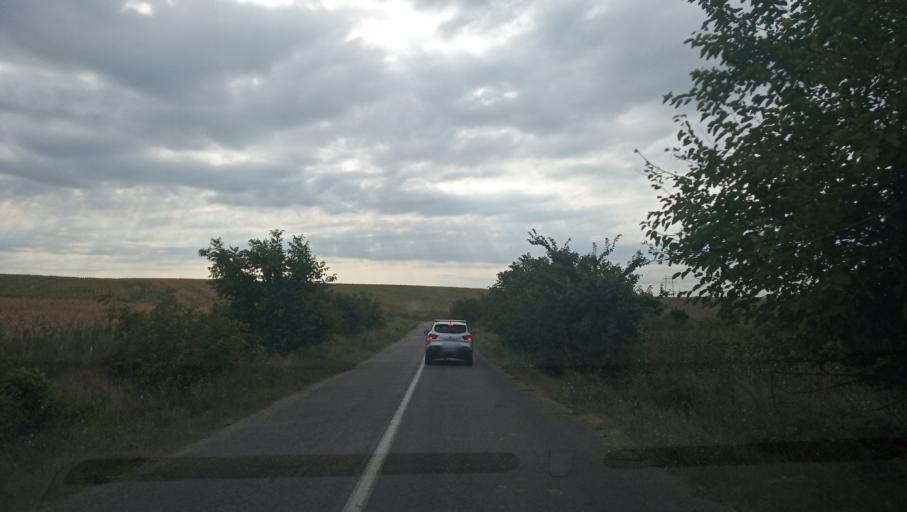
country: RO
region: Constanta
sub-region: Comuna Adamclisi
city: Adamclisi
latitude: 44.0283
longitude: 27.9779
